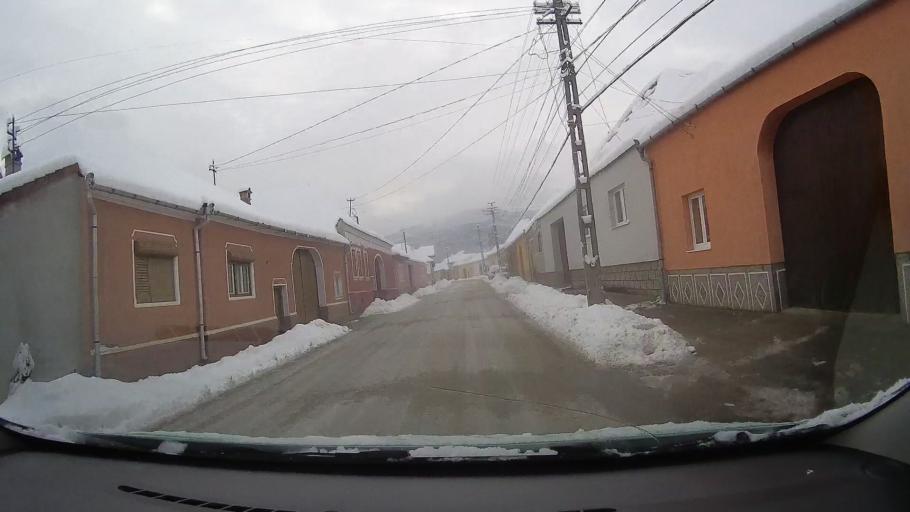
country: RO
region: Alba
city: Pianu de Sus
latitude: 45.9014
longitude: 23.4805
